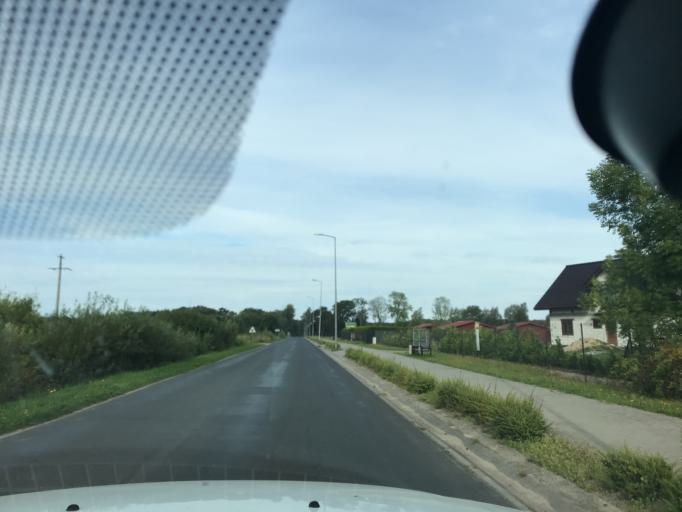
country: PL
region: West Pomeranian Voivodeship
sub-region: Powiat slawienski
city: Slawno
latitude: 54.5338
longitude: 16.5780
